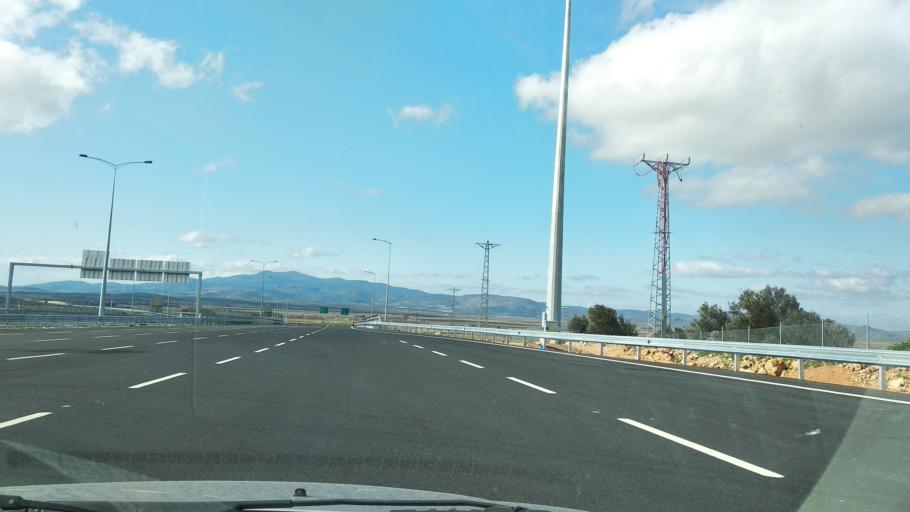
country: TR
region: Izmir
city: Zeytindag
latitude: 38.9737
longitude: 27.0525
